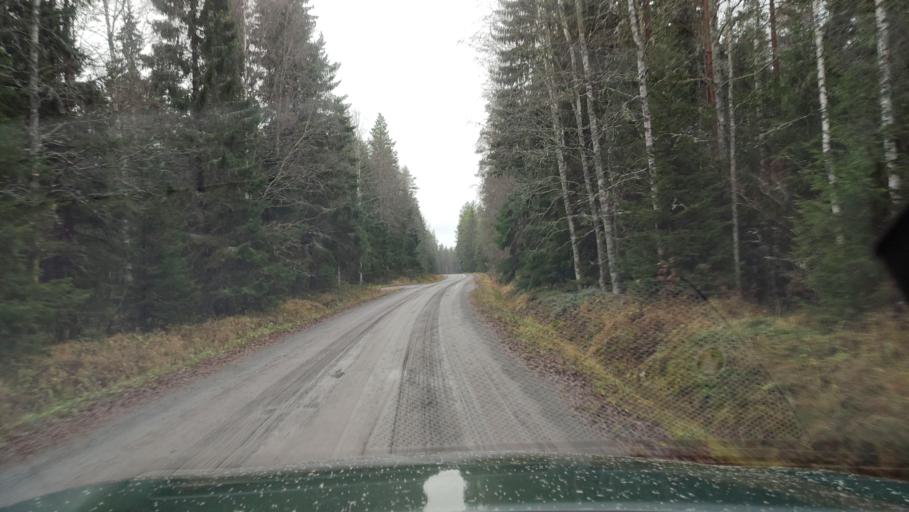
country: FI
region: Ostrobothnia
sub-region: Sydosterbotten
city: Naerpes
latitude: 62.4547
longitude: 21.4794
